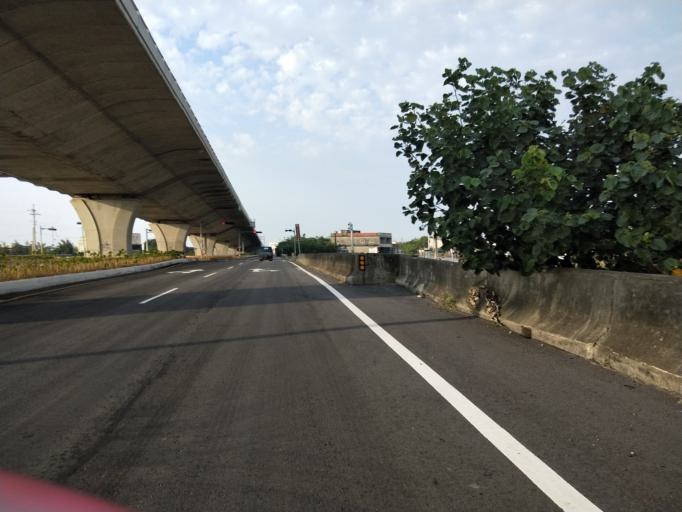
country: TW
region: Taiwan
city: Fengyuan
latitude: 24.3597
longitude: 120.5854
